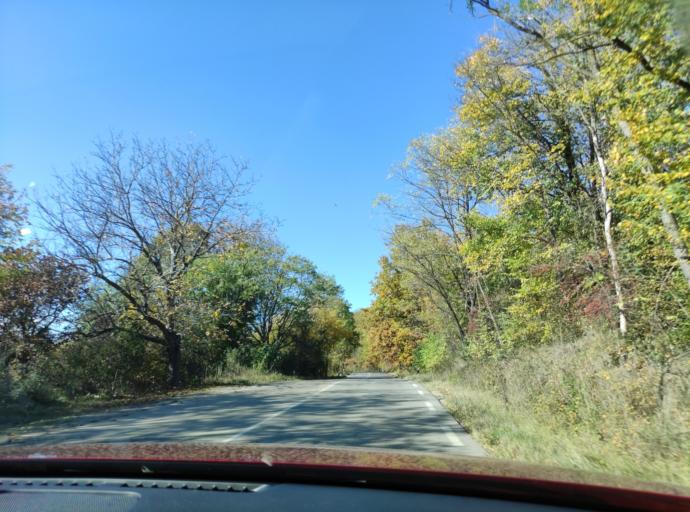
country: BG
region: Montana
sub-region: Obshtina Montana
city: Montana
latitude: 43.4059
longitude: 23.0661
